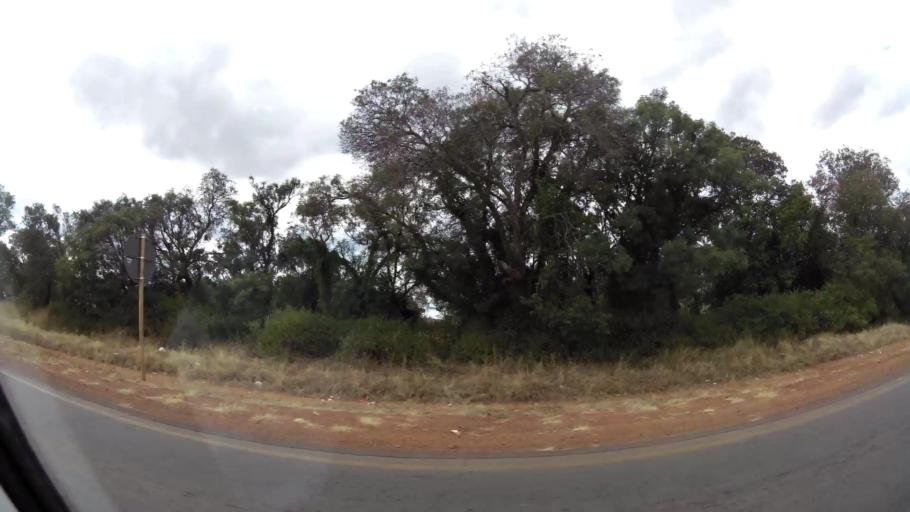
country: ZA
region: Limpopo
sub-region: Waterberg District Municipality
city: Modimolle
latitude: -24.7297
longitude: 28.4299
